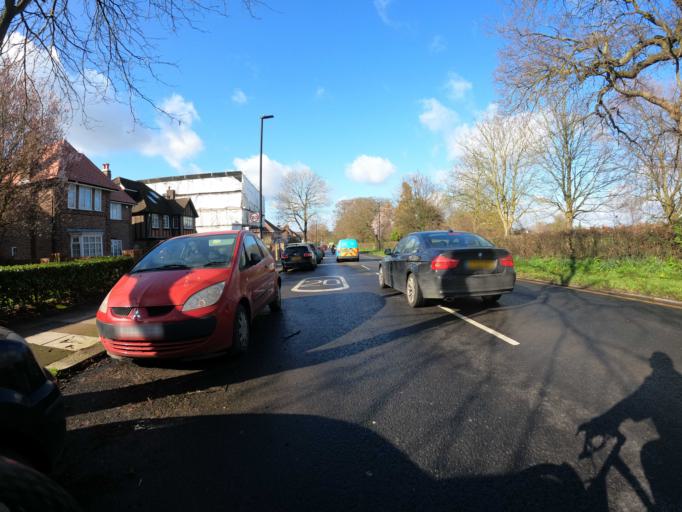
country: GB
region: England
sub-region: Greater London
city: Ealing Broadway
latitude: 51.5224
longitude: -0.3234
